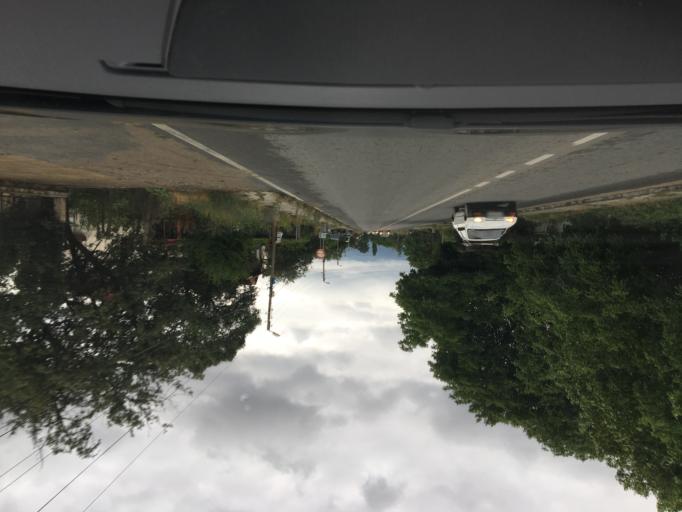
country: BG
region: Kyustendil
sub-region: Obshtina Kyustendil
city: Kyustendil
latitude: 42.2786
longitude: 22.7373
